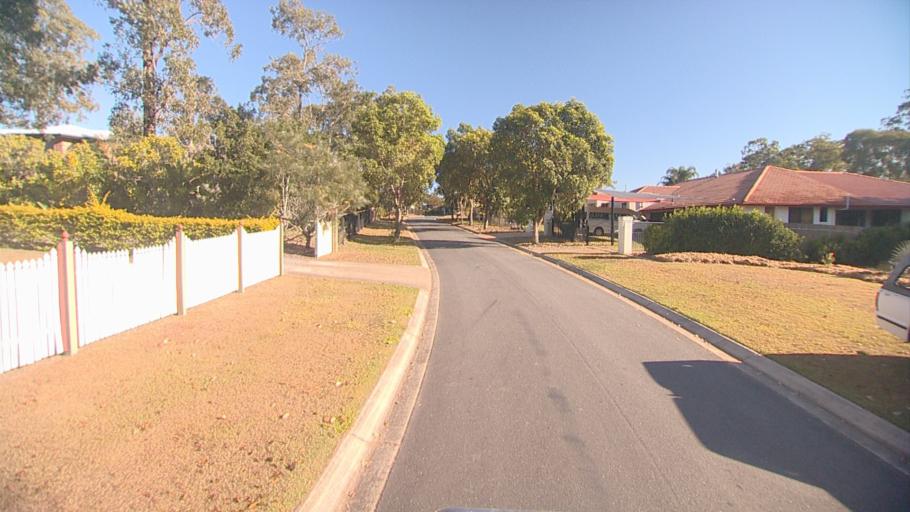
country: AU
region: Queensland
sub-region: Brisbane
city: Forest Lake
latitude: -27.6597
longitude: 152.9957
